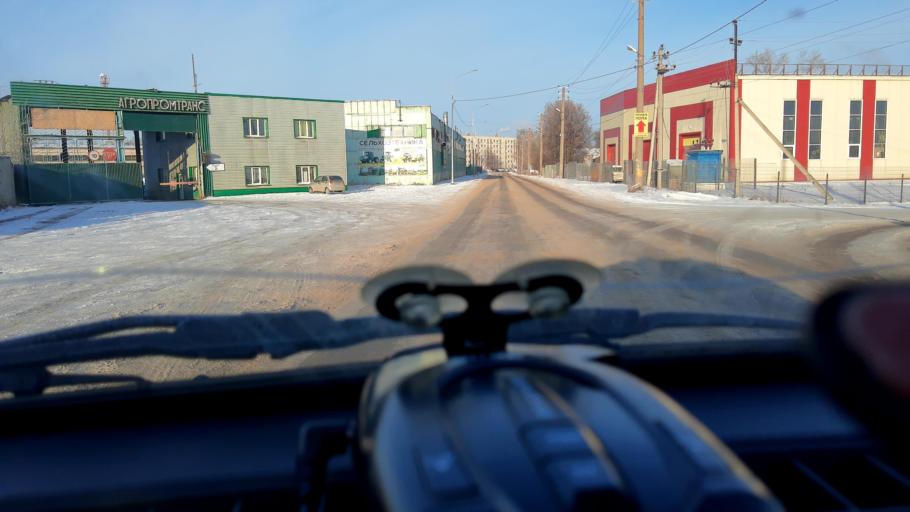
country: RU
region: Bashkortostan
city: Avdon
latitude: 54.6065
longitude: 55.8454
